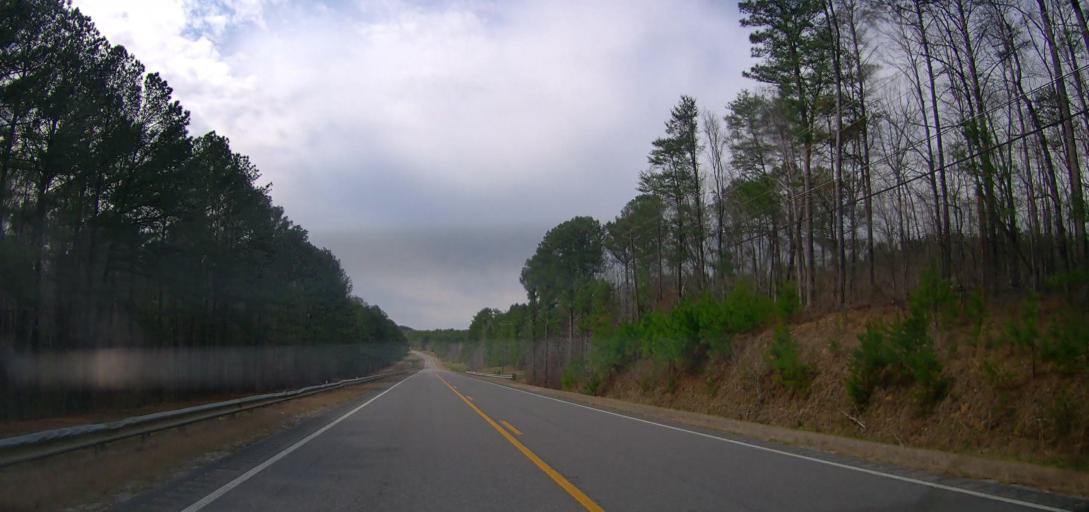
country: US
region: Alabama
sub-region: Walker County
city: Carbon Hill
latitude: 33.9197
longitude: -87.5812
